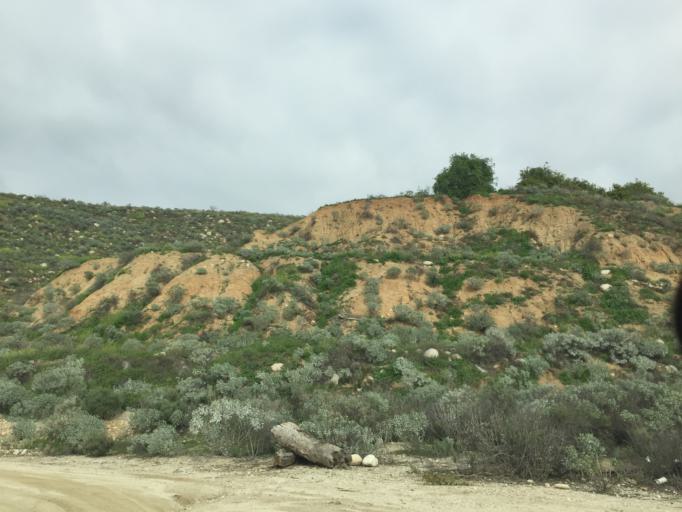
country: US
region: California
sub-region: San Bernardino County
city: Mentone
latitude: 34.1079
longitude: -117.1261
